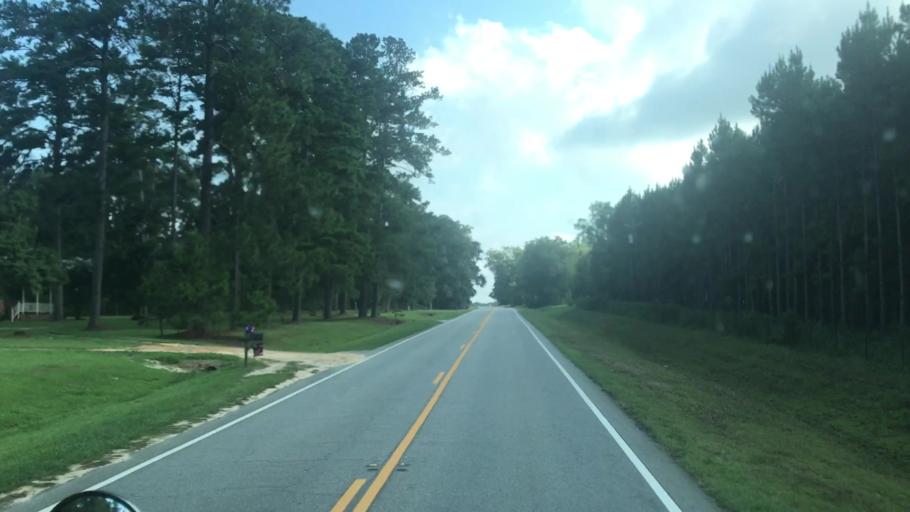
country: US
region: Georgia
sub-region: Decatur County
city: Bainbridge
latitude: 30.7683
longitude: -84.4881
